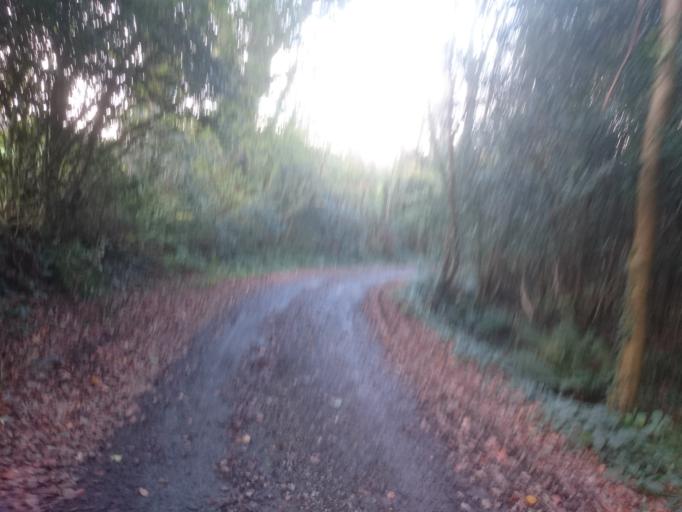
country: IE
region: Leinster
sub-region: Kilkenny
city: Thomastown
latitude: 52.4645
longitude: -7.0589
